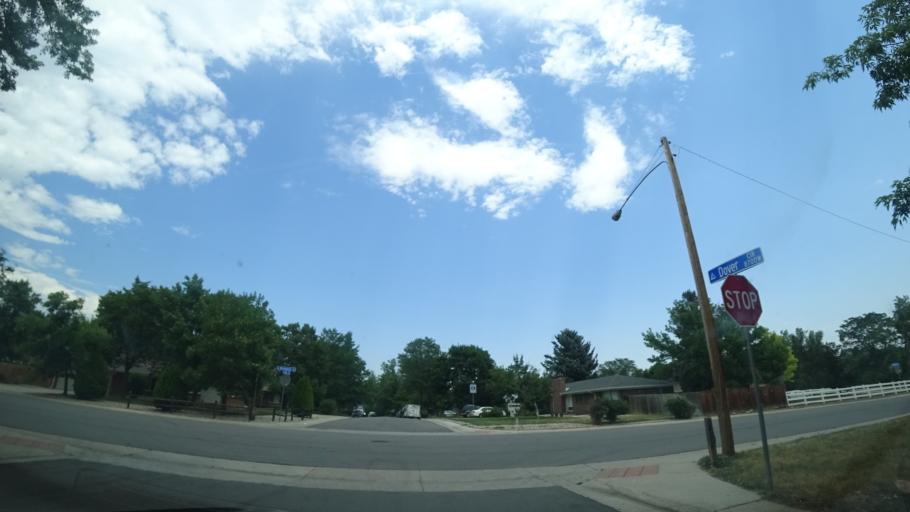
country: US
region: Colorado
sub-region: Jefferson County
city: Lakewood
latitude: 39.7217
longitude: -105.0945
